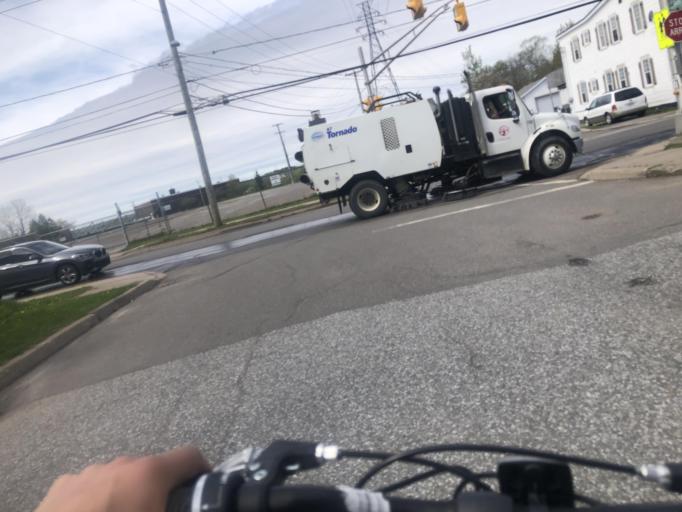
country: CA
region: New Brunswick
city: Saint John
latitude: 45.2830
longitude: -66.0822
